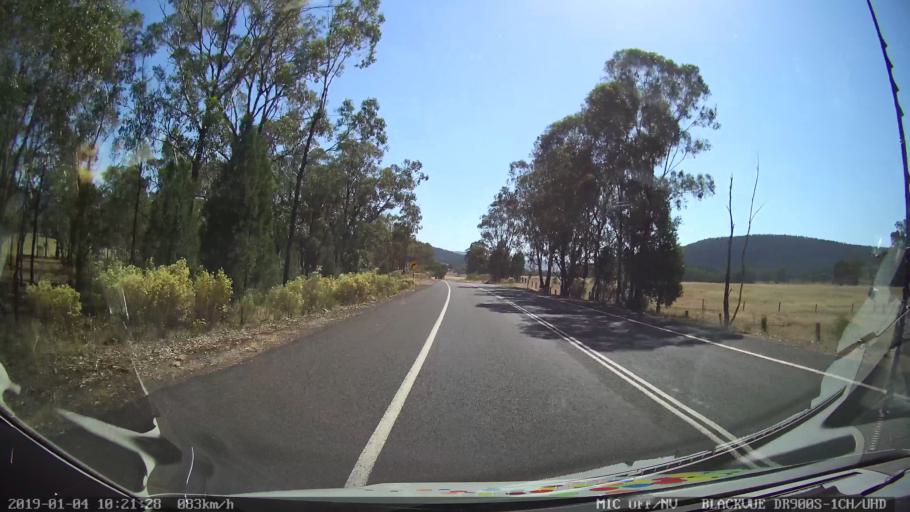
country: AU
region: New South Wales
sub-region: Cabonne
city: Canowindra
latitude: -33.3727
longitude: 148.5108
